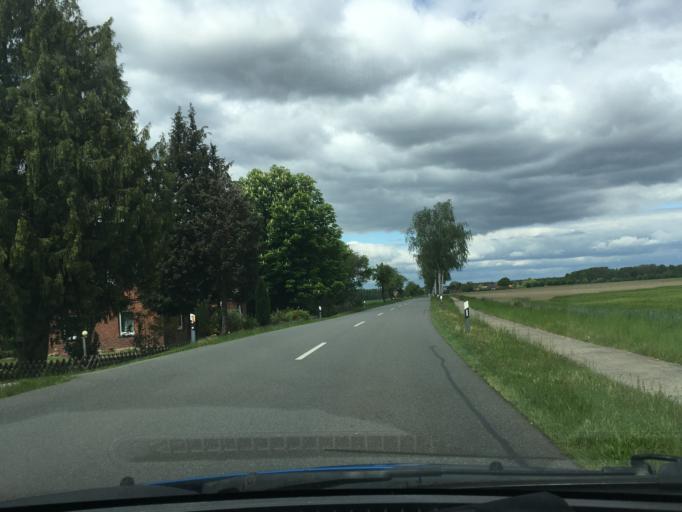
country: DE
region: Lower Saxony
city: Suderburg
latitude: 52.9114
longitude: 10.4218
